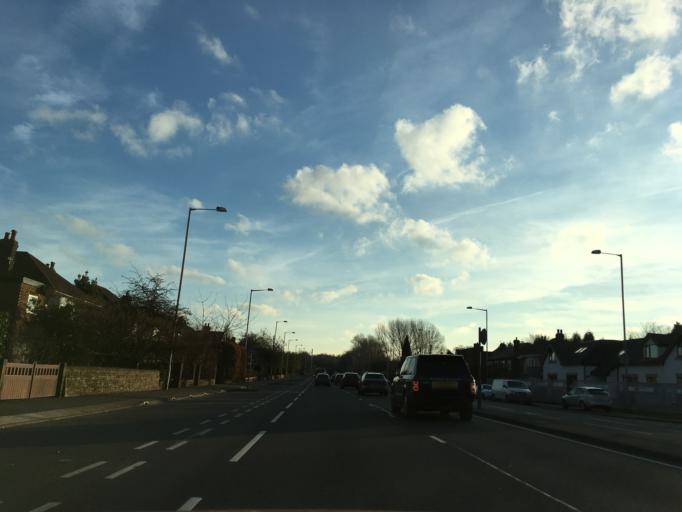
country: GB
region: England
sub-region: Manchester
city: Didsbury
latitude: 53.3899
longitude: -2.2258
